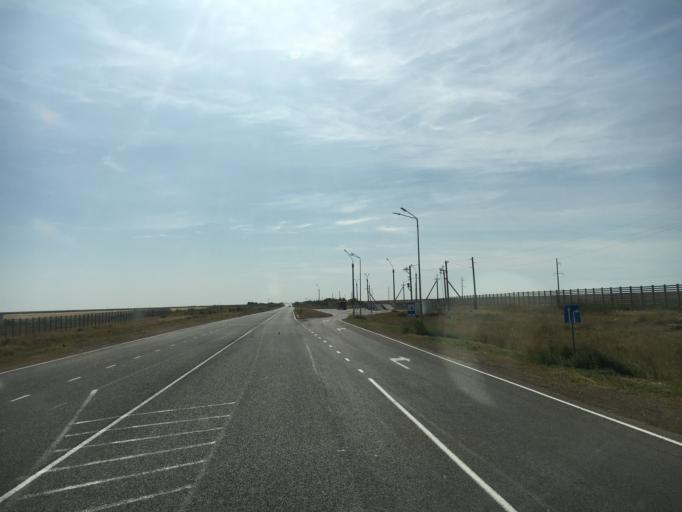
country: KZ
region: Batys Qazaqstan
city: Peremetnoe
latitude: 51.1339
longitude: 50.9034
